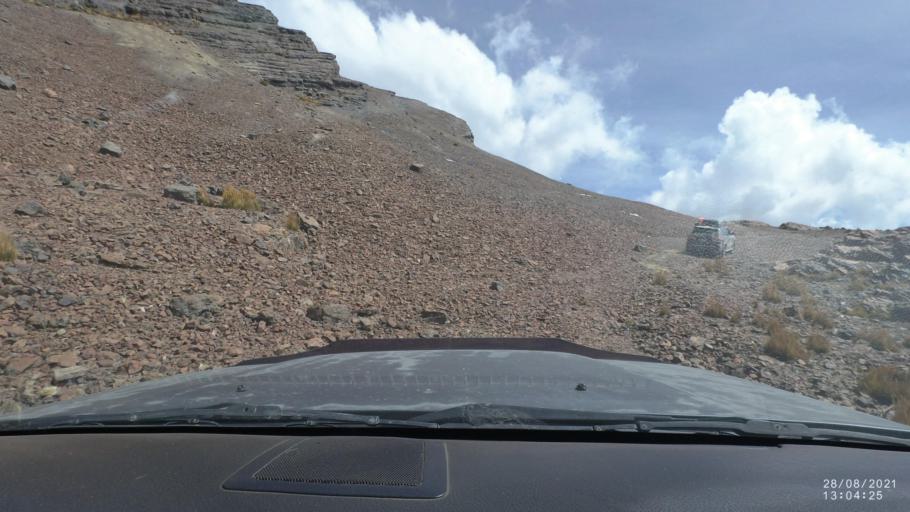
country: BO
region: Cochabamba
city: Sipe Sipe
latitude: -17.2831
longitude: -66.3880
